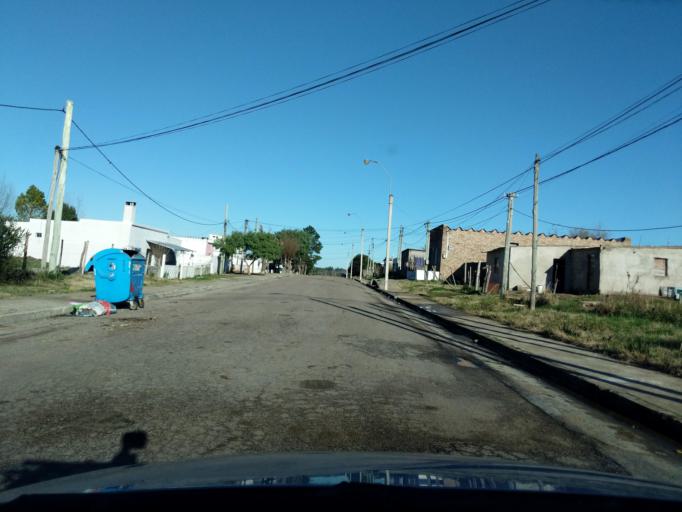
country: UY
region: Florida
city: Florida
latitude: -34.1005
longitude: -56.2402
